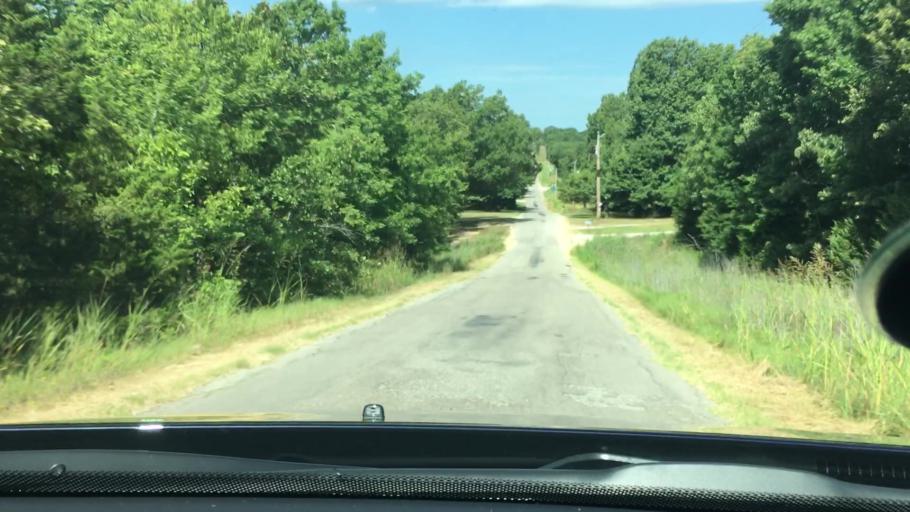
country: US
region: Oklahoma
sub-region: Pontotoc County
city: Ada
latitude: 34.7635
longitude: -96.5716
